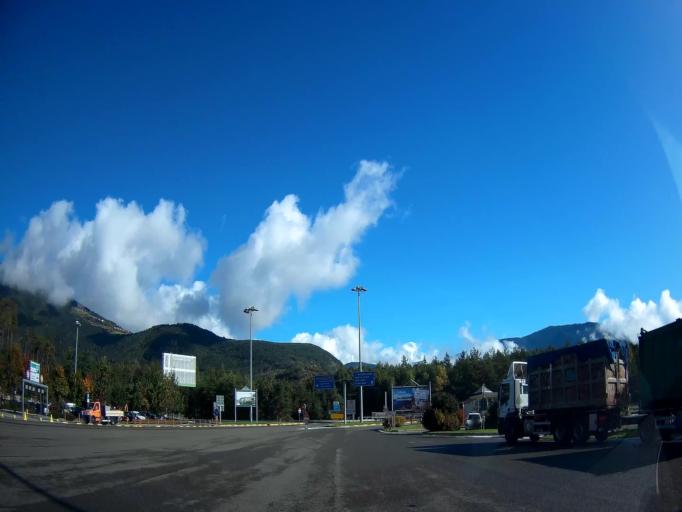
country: IT
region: Trentino-Alto Adige
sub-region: Bolzano
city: Naz-Sciaves - Natz-Schabs
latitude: 46.7640
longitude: 11.6423
